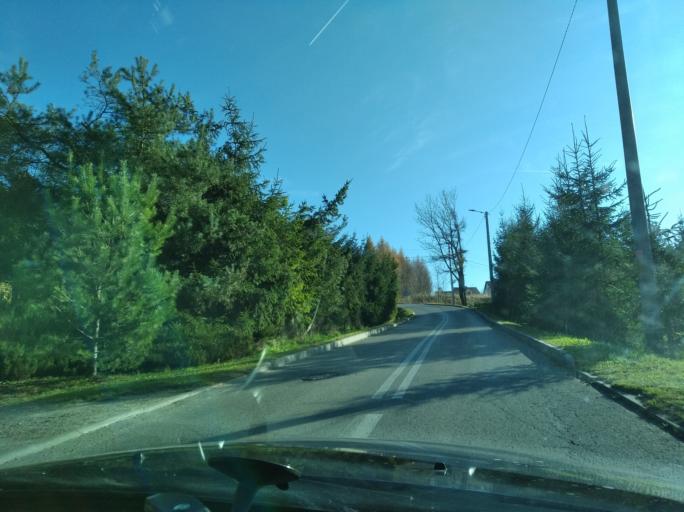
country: PL
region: Subcarpathian Voivodeship
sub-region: Powiat rzeszowski
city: Niechobrz
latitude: 49.9915
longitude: 21.8785
